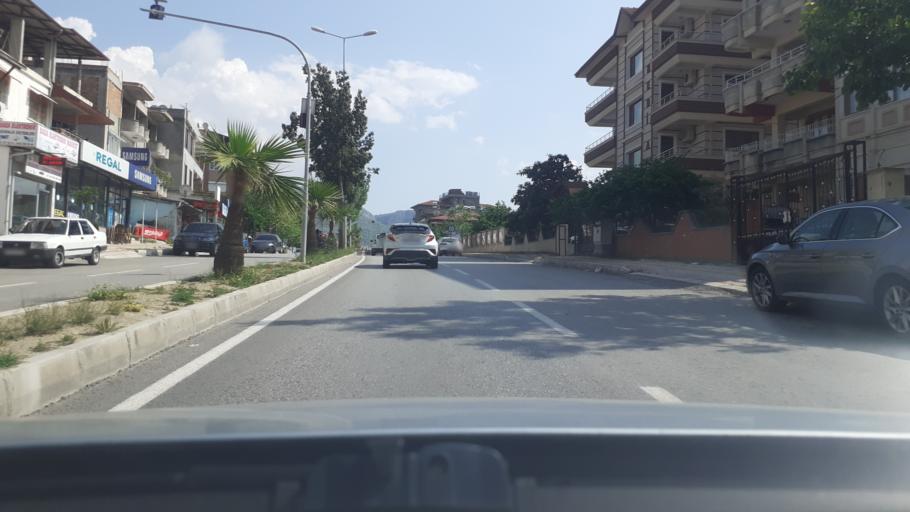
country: TR
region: Hatay
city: Gumusgoze
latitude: 36.1428
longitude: 36.1412
